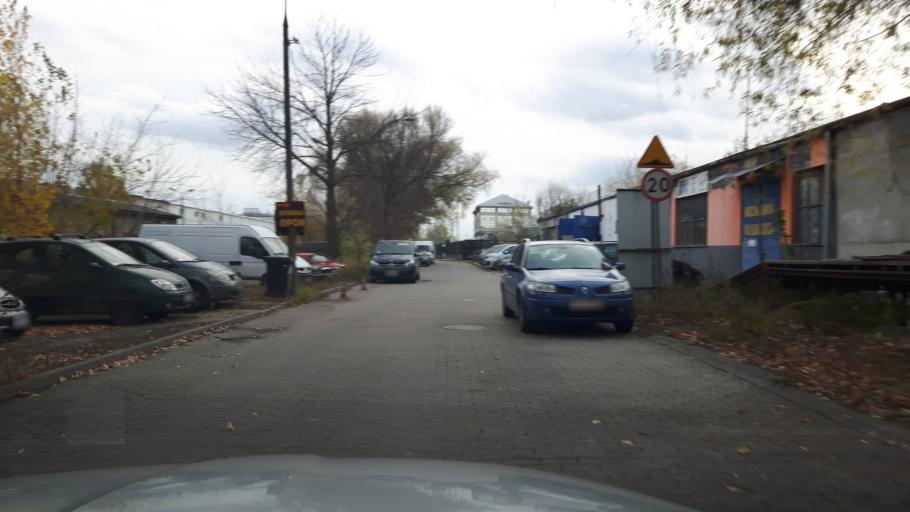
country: PL
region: Masovian Voivodeship
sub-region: Warszawa
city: Wlochy
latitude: 52.1748
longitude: 20.9905
